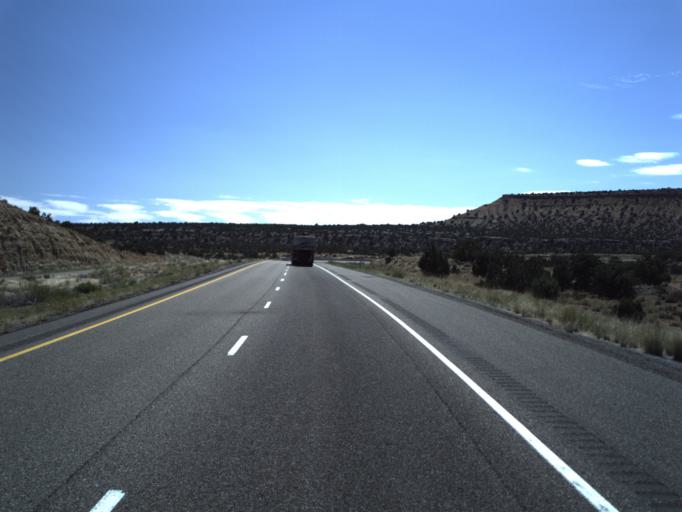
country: US
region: Utah
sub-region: Emery County
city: Castle Dale
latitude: 38.9195
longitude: -110.5016
